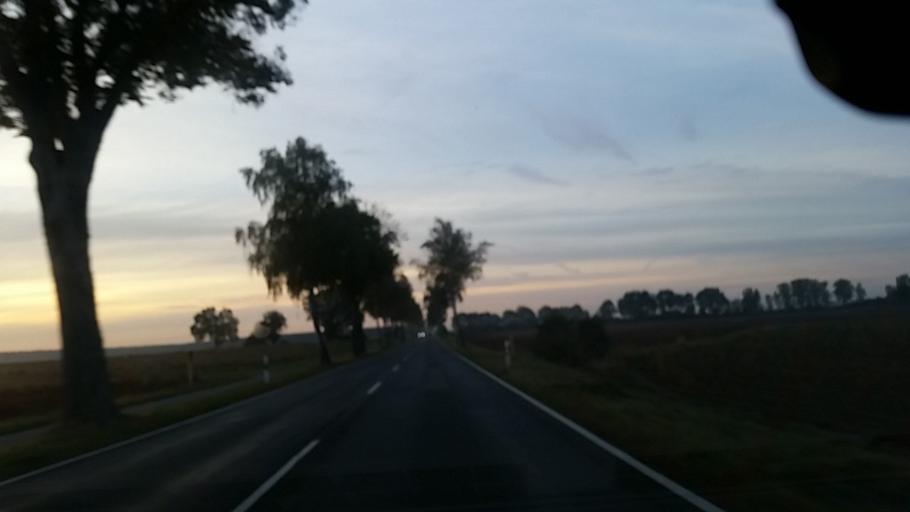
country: DE
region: Lower Saxony
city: Bodenteich
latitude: 52.8231
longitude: 10.6878
